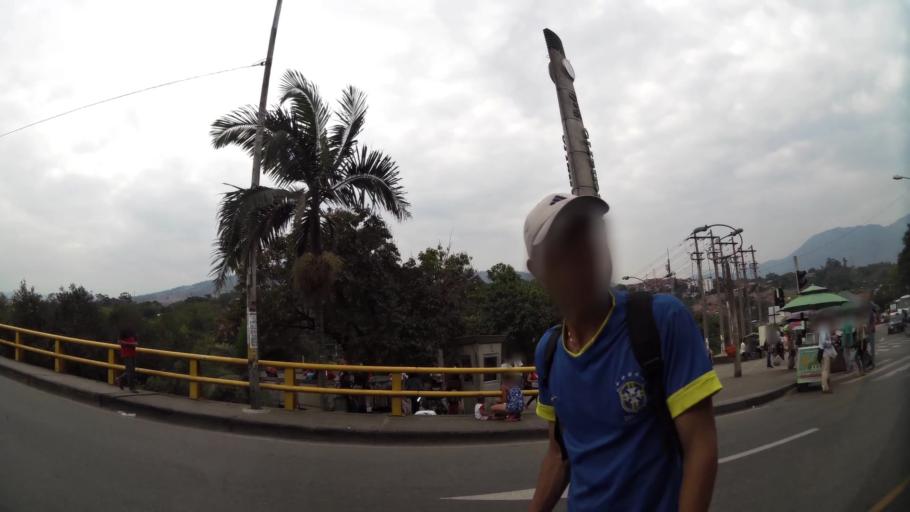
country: CO
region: Antioquia
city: Medellin
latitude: 6.2903
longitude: -75.5630
